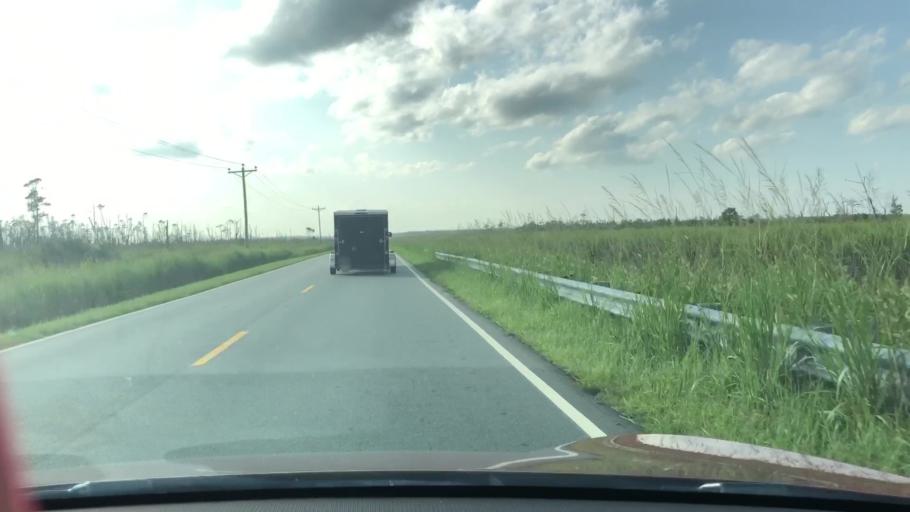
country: US
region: North Carolina
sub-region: Dare County
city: Wanchese
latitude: 35.6244
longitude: -75.8443
